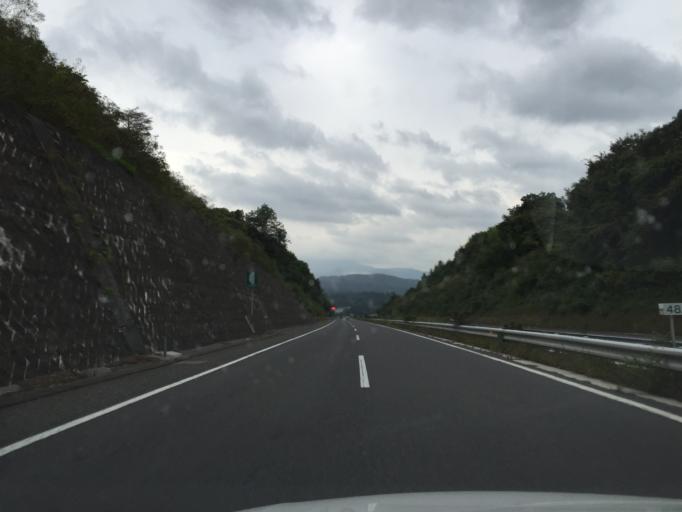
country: JP
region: Fukushima
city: Funehikimachi-funehiki
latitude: 37.3978
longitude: 140.5776
